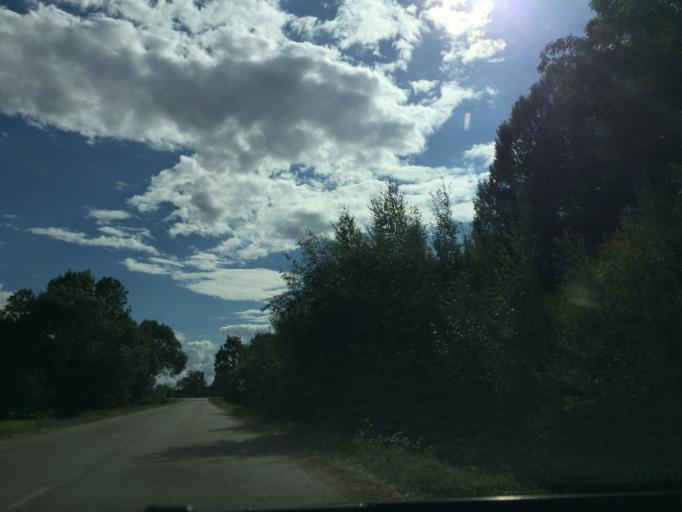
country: LT
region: Siauliu apskritis
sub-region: Joniskis
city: Joniskis
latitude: 56.2475
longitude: 23.5550
